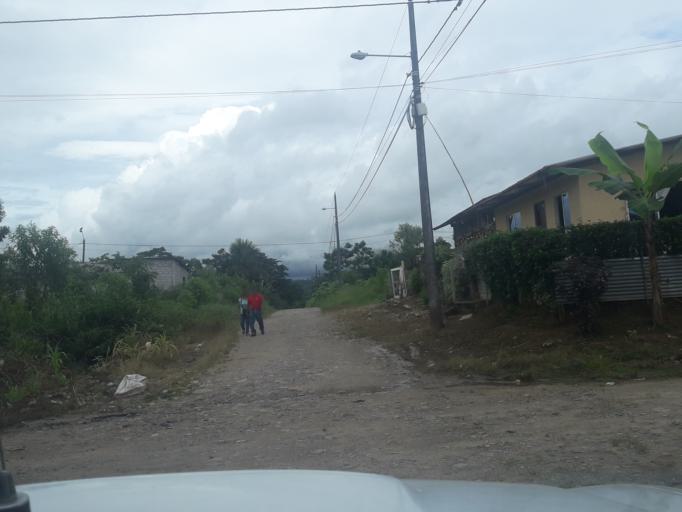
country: EC
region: Napo
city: Archidona
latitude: -0.9477
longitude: -77.8149
